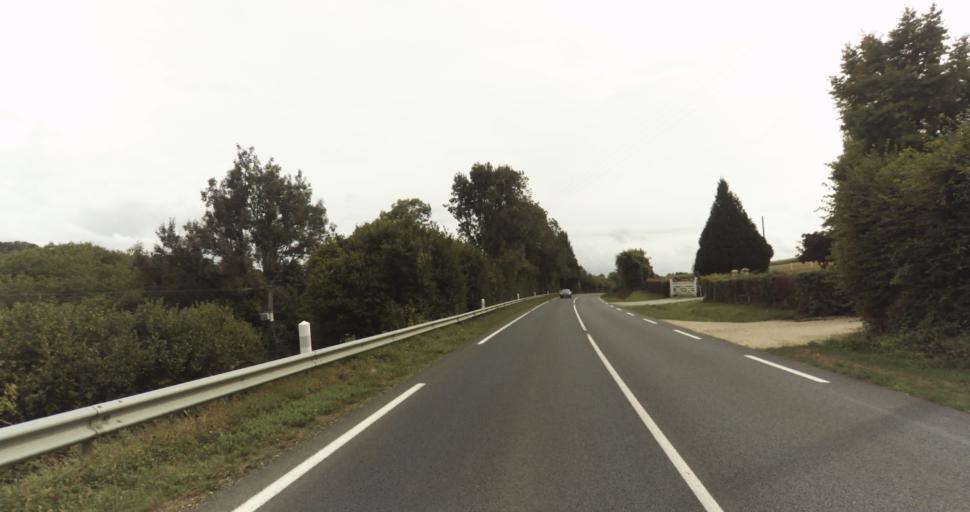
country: FR
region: Lower Normandy
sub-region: Departement de l'Orne
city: Gace
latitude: 48.8219
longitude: 0.2802
